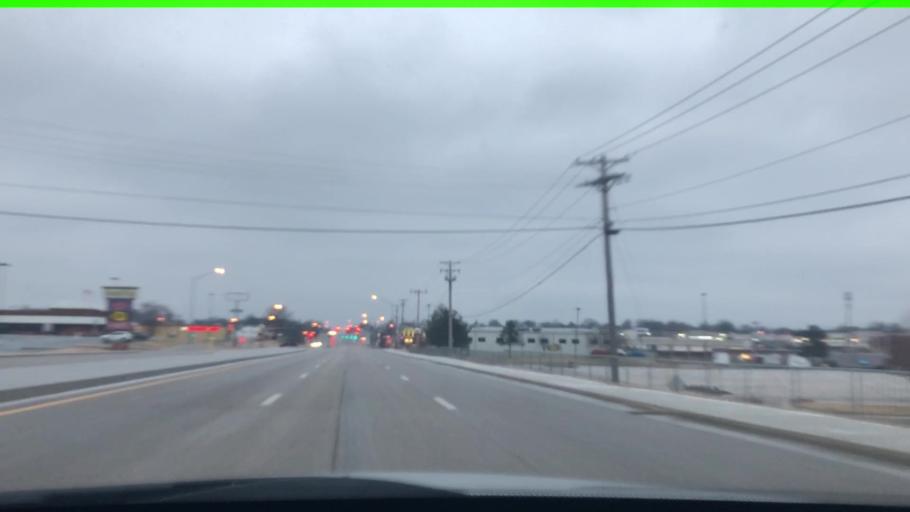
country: US
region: Missouri
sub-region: Boone County
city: Columbia
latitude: 38.9636
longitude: -92.3714
